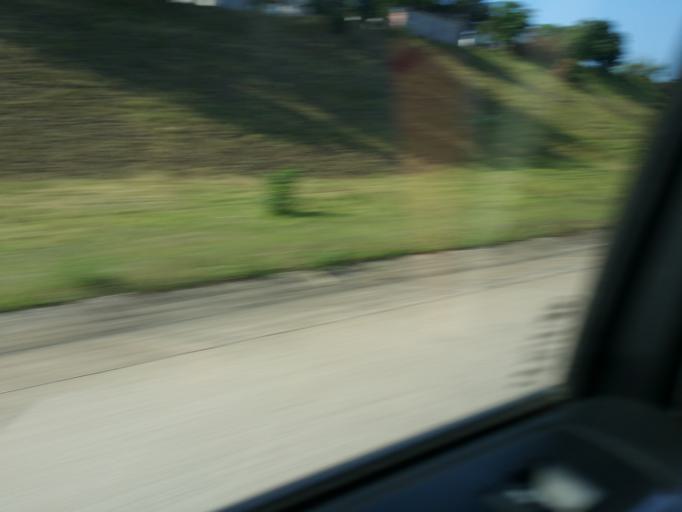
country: ZA
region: KwaZulu-Natal
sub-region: iLembe District Municipality
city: Stanger
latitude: -29.3781
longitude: 31.2957
